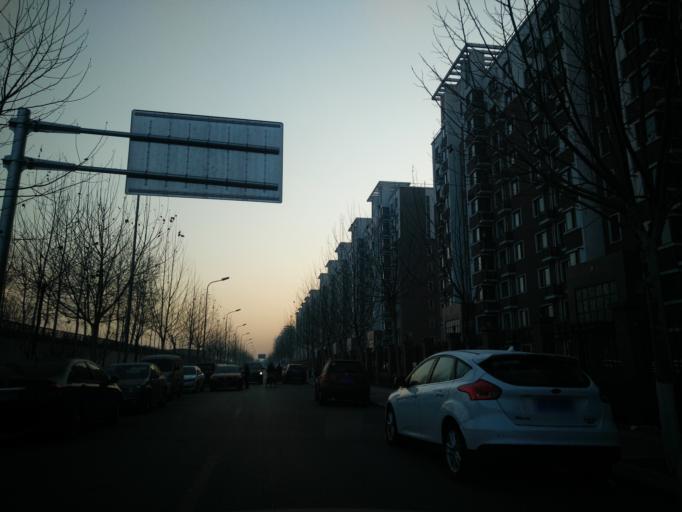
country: CN
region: Beijing
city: Xingfeng
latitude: 39.7173
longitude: 116.3917
